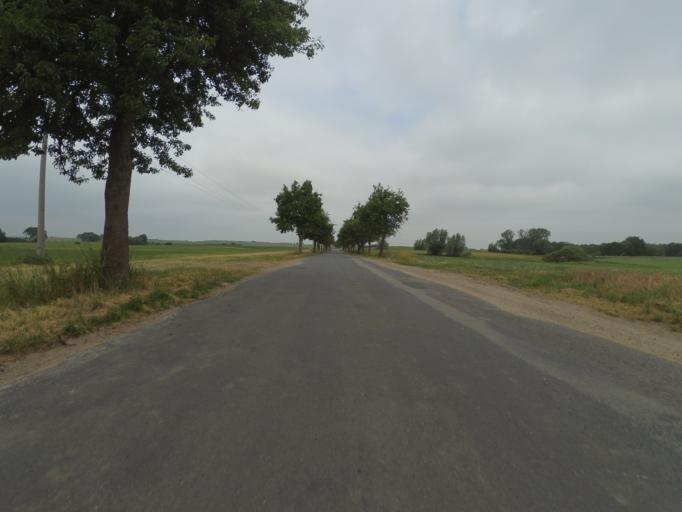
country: DE
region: Mecklenburg-Vorpommern
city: Goldberg
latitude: 53.5121
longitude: 12.1163
